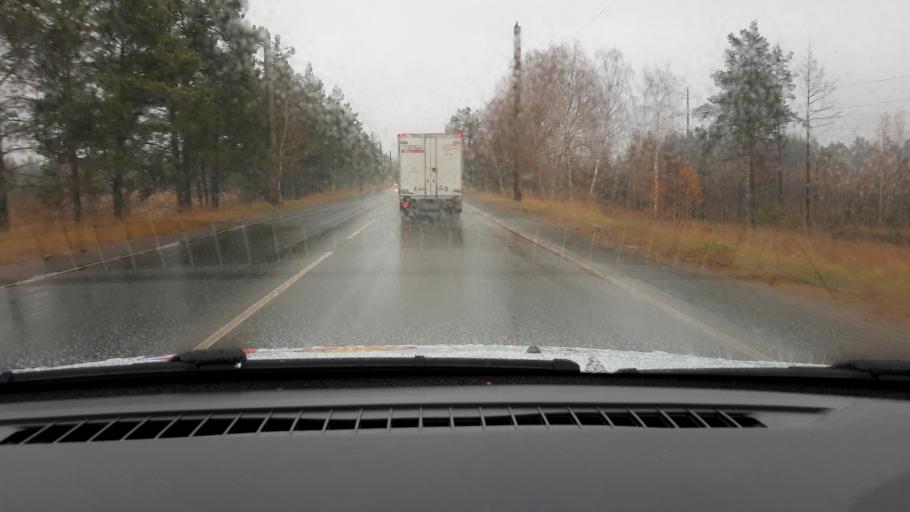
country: RU
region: Nizjnij Novgorod
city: Babino
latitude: 56.2797
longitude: 43.5679
